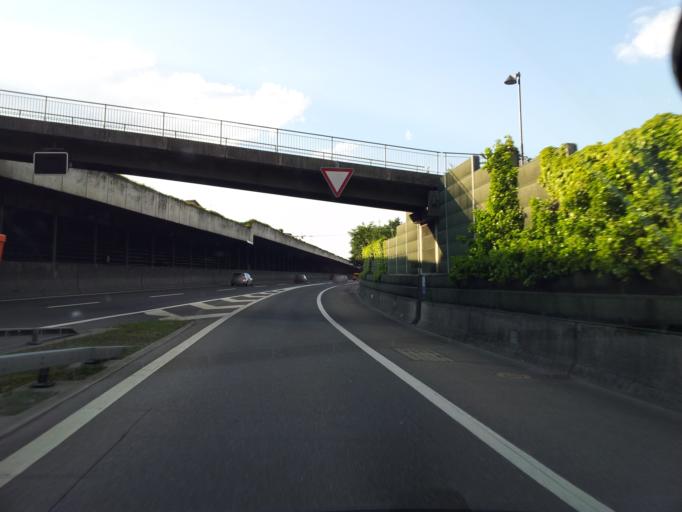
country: CH
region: Nidwalden
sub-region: Nidwalden
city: Hergiswil
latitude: 46.9826
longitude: 8.3078
